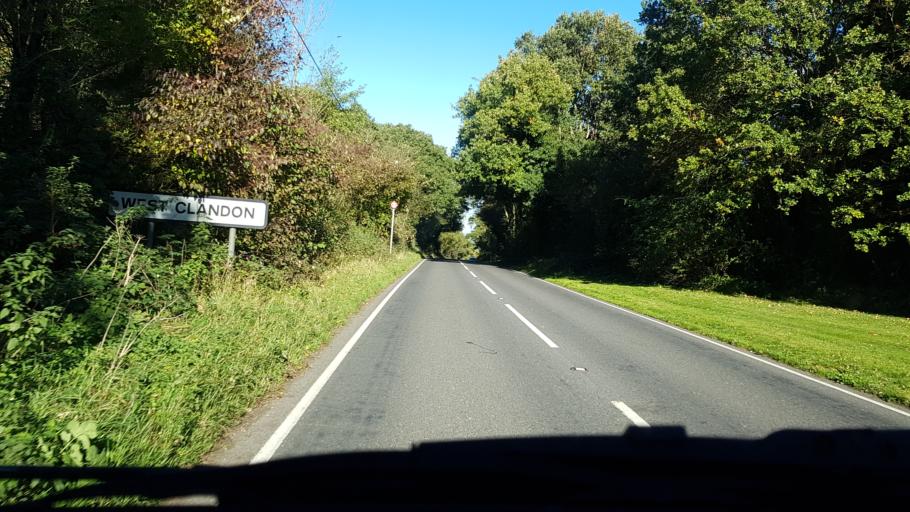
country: GB
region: England
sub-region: Surrey
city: Chilworth
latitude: 51.2373
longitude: -0.5063
